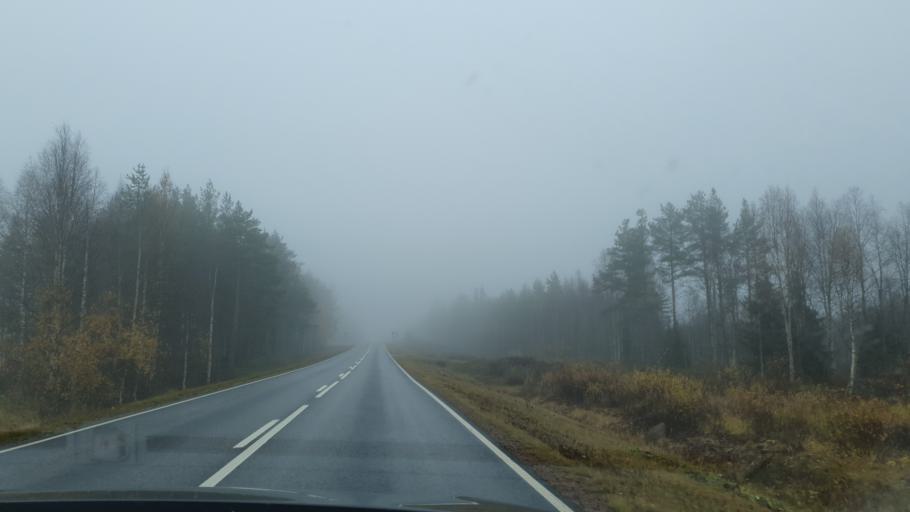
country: FI
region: Lapland
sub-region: Rovaniemi
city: Rovaniemi
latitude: 66.7933
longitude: 25.4154
